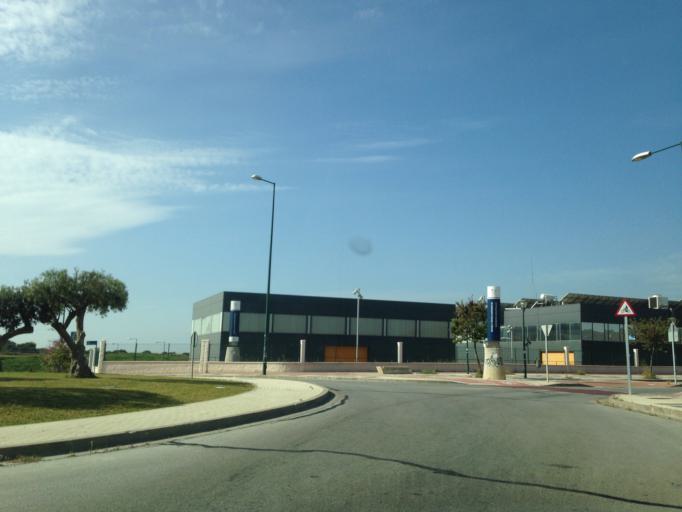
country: ES
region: Andalusia
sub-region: Provincia de Malaga
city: Malaga
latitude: 36.7164
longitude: -4.4899
